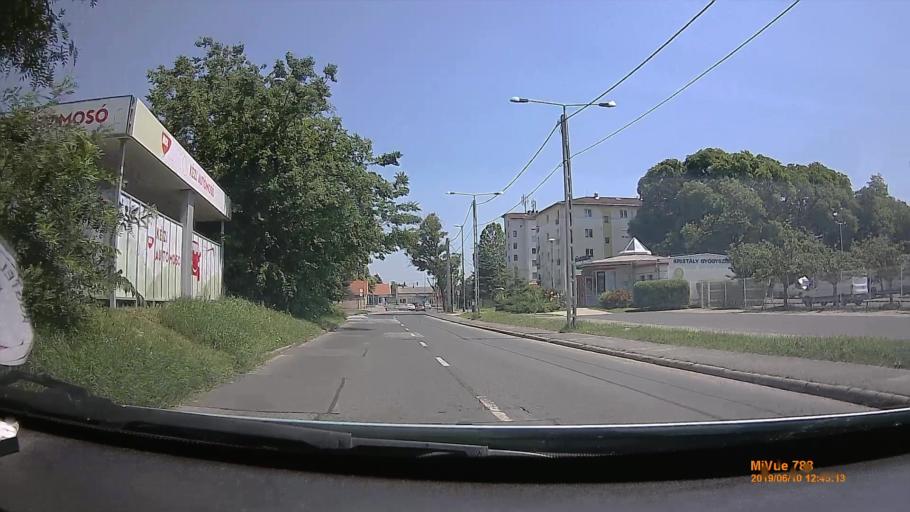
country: HU
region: Borsod-Abauj-Zemplen
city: Miskolc
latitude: 48.1008
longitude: 20.7288
